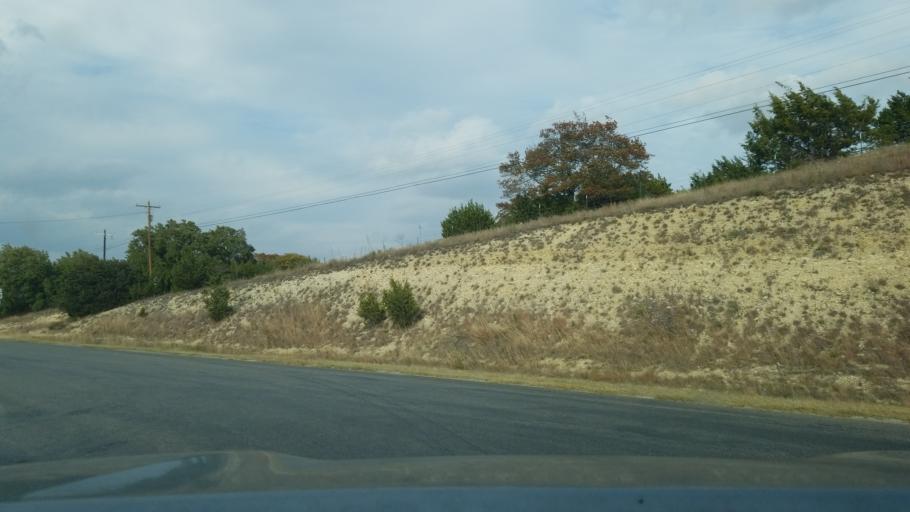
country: US
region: Texas
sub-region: Mills County
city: Goldthwaite
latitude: 31.4673
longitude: -98.5680
